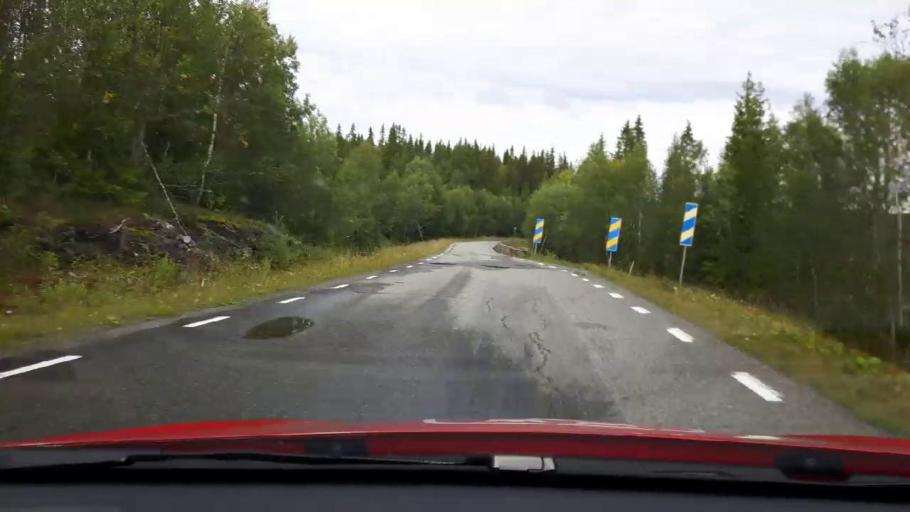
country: SE
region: Jaemtland
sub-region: Are Kommun
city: Are
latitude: 63.7432
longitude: 13.0799
